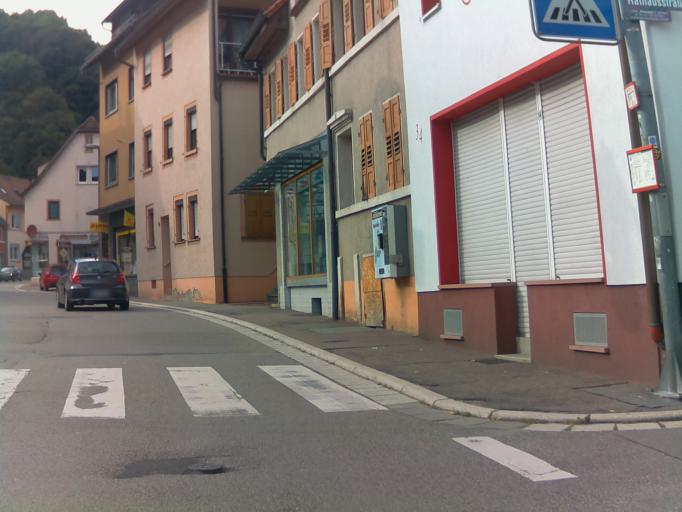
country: DE
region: Baden-Wuerttemberg
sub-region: Karlsruhe Region
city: Schonau
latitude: 49.4348
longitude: 8.8096
